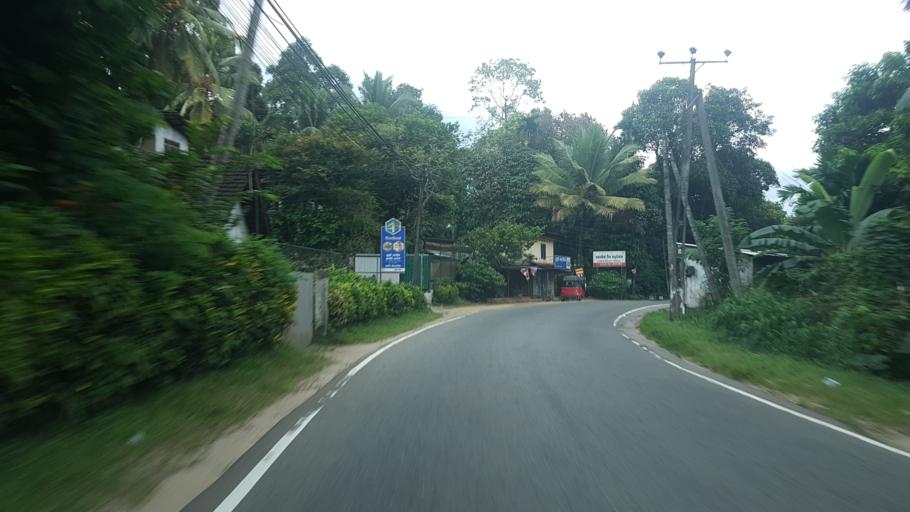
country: LK
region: Western
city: Hanwella Ihala
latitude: 7.0334
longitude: 80.2854
